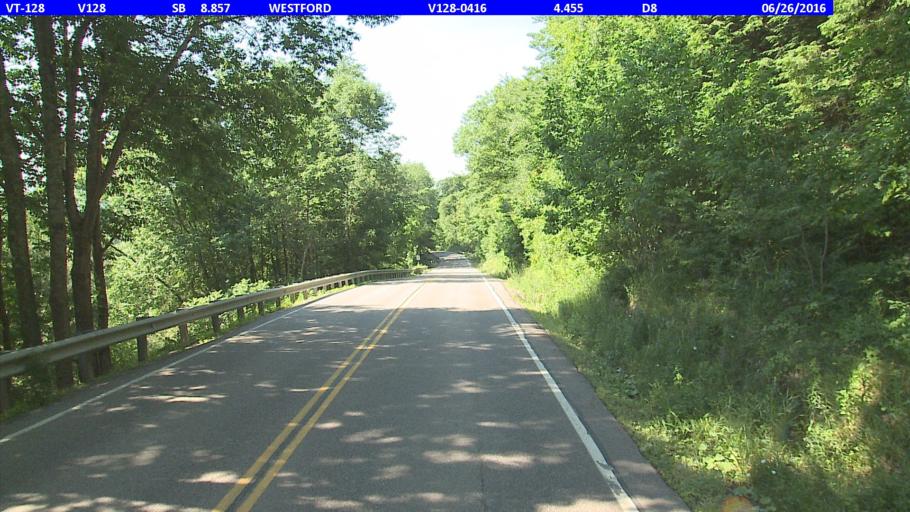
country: US
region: Vermont
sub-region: Chittenden County
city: Milton
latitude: 44.6186
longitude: -73.0156
